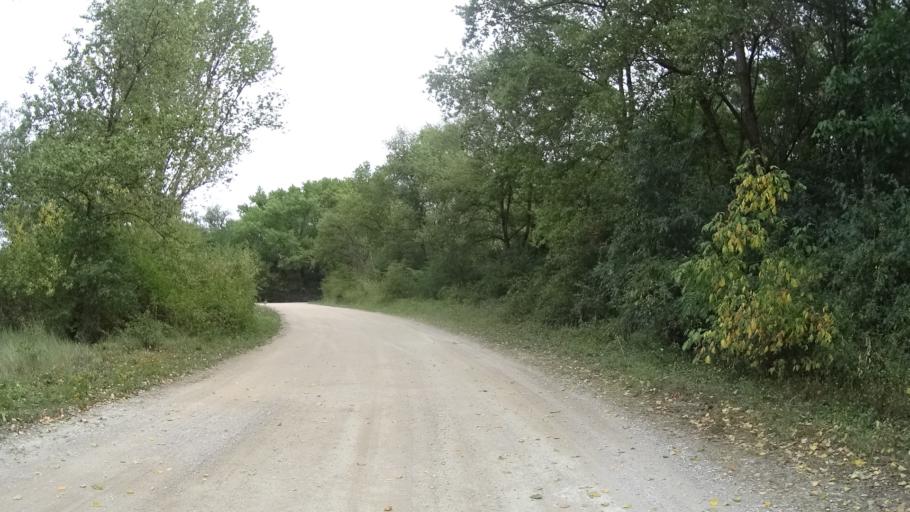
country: FR
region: Centre
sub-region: Departement du Loiret
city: Baule
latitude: 47.7905
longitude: 1.6656
